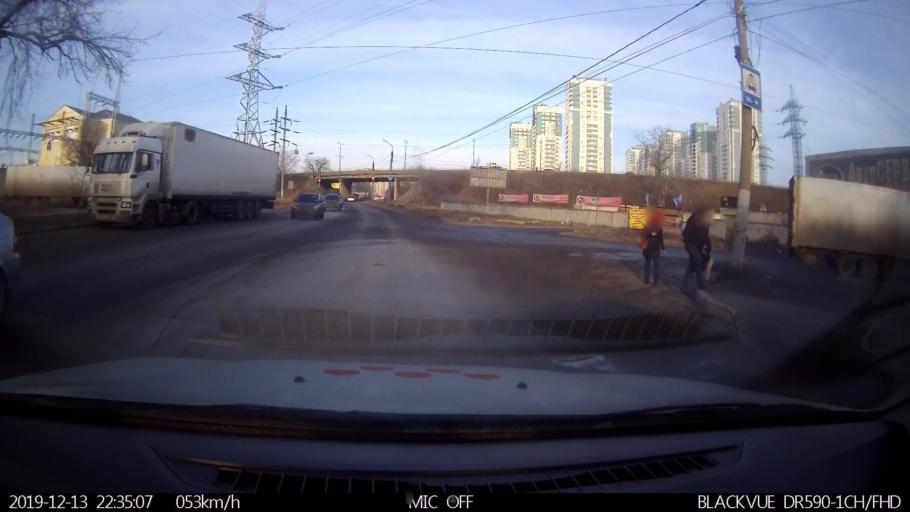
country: RU
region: Nizjnij Novgorod
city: Nizhniy Novgorod
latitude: 56.2974
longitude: 43.9509
